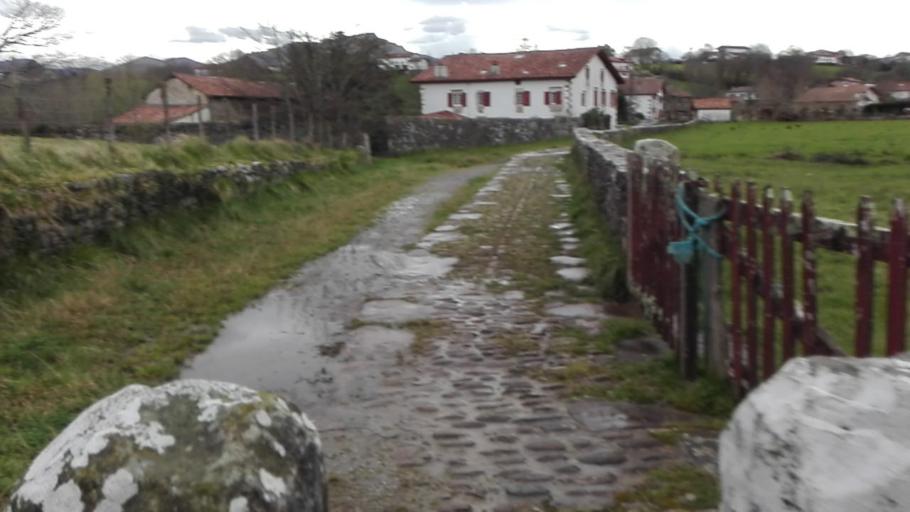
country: FR
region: Aquitaine
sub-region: Departement des Pyrenees-Atlantiques
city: Sare
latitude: 43.3099
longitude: -1.5800
